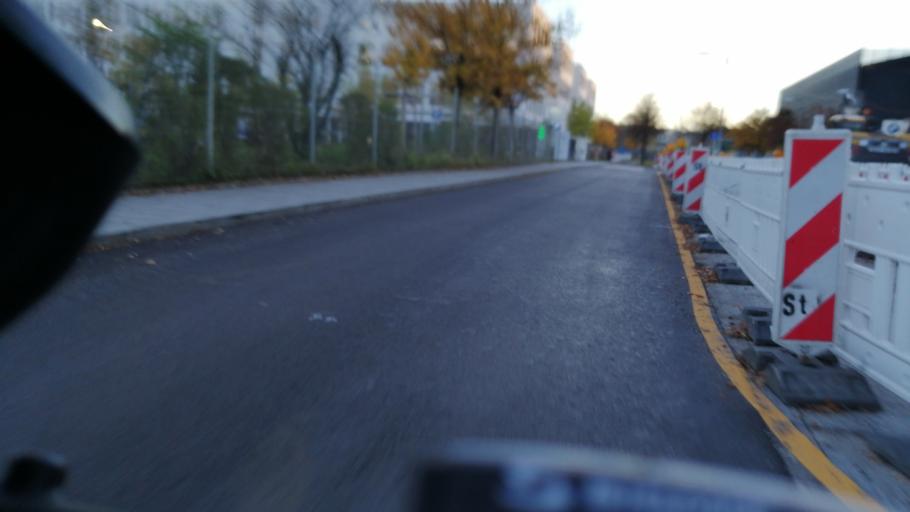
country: DE
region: Bavaria
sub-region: Upper Bavaria
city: Unterfoehring
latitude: 48.1938
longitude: 11.6083
